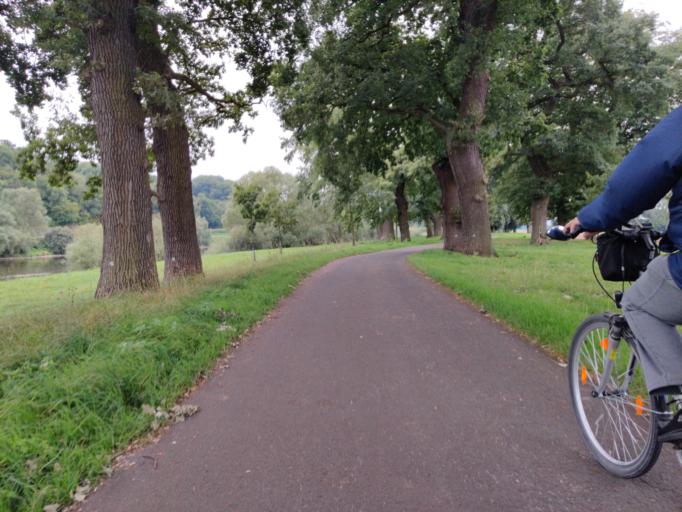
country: DE
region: North Rhine-Westphalia
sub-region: Regierungsbezirk Detmold
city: Hoexter
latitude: 51.7742
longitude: 9.4111
